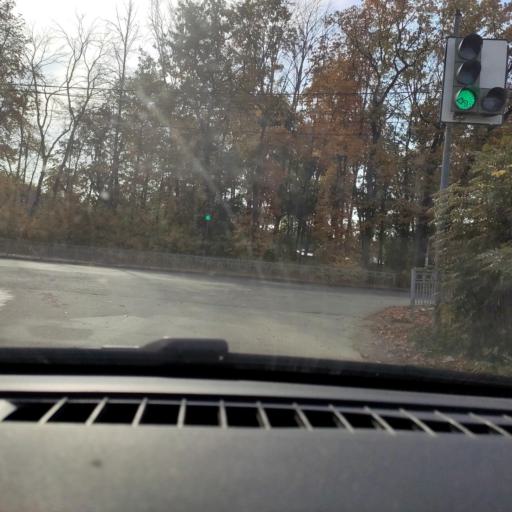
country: RU
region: Voronezj
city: Voronezh
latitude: 51.7266
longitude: 39.2124
